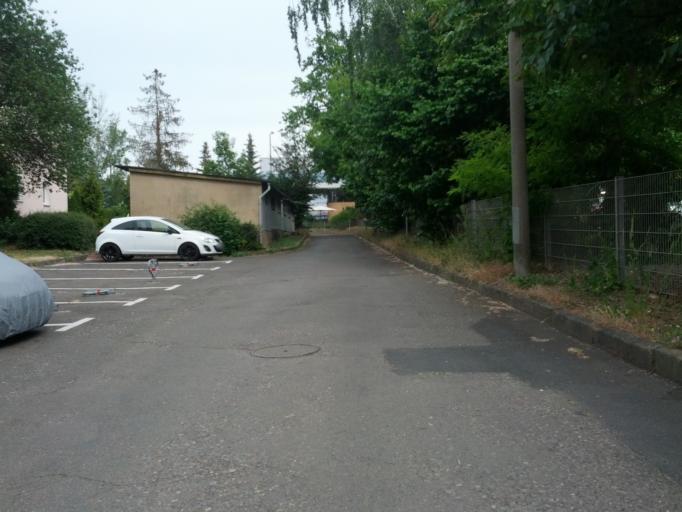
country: DE
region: Thuringia
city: Eisenach
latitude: 50.9895
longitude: 10.3137
